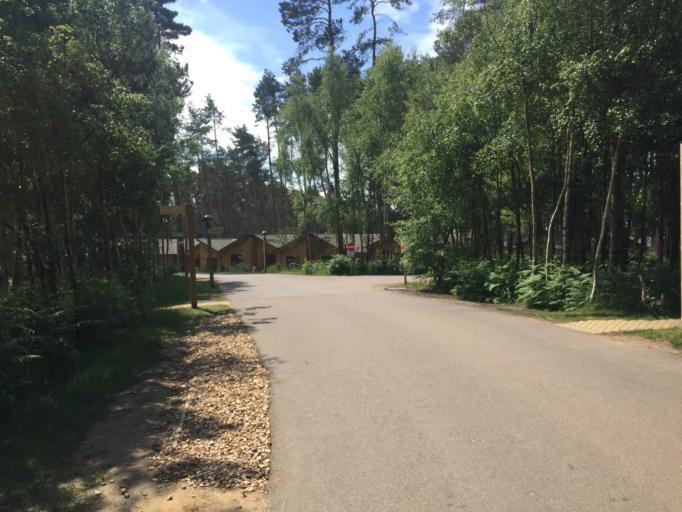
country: GB
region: England
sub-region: Central Bedfordshire
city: Millbrook
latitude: 52.0266
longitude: -0.5369
